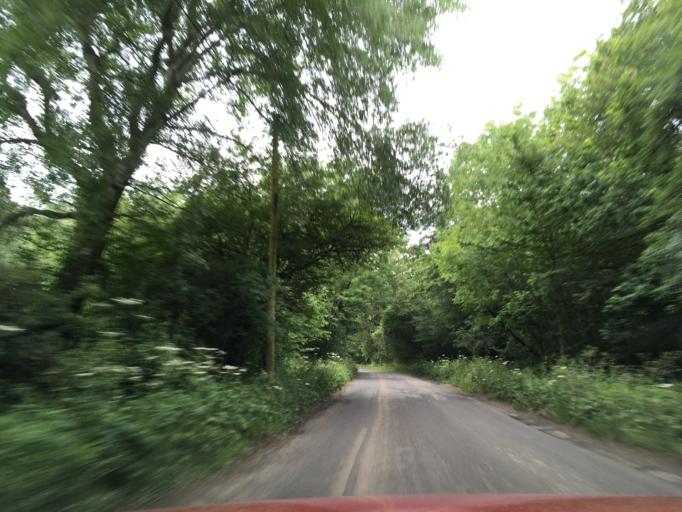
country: GB
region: England
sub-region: Wiltshire
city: Norton
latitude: 51.5907
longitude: -2.1779
